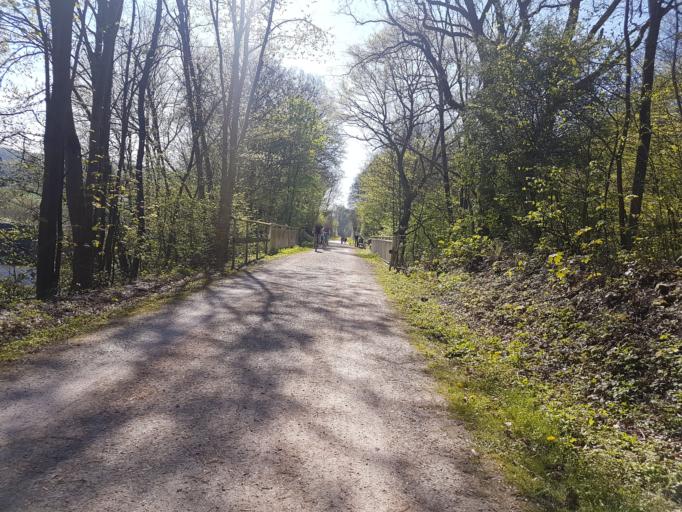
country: DE
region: North Rhine-Westphalia
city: Hattingen
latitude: 51.3872
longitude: 7.1889
